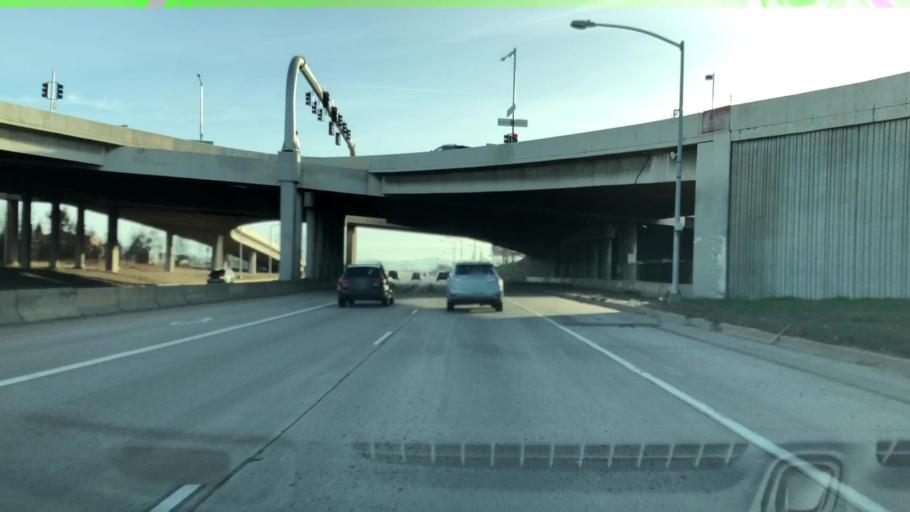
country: US
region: Colorado
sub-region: Arapahoe County
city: Englewood
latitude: 39.6790
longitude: -104.9935
